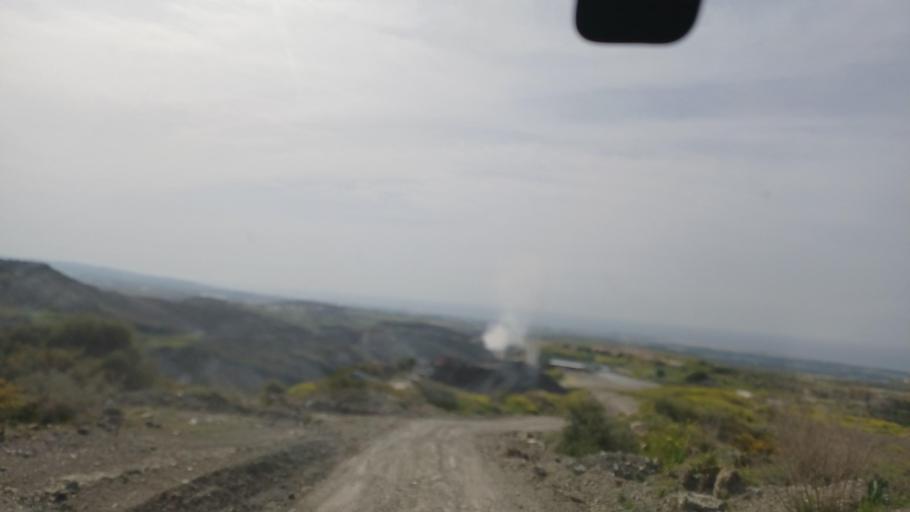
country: CY
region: Pafos
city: Mesogi
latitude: 34.7778
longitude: 32.4824
